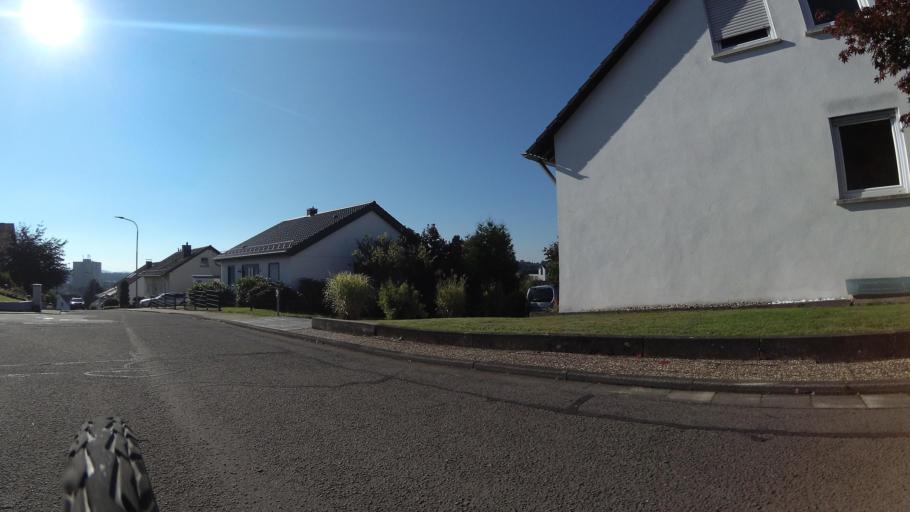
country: DE
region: Rheinland-Pfalz
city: Waldmohr
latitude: 49.3921
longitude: 7.3333
